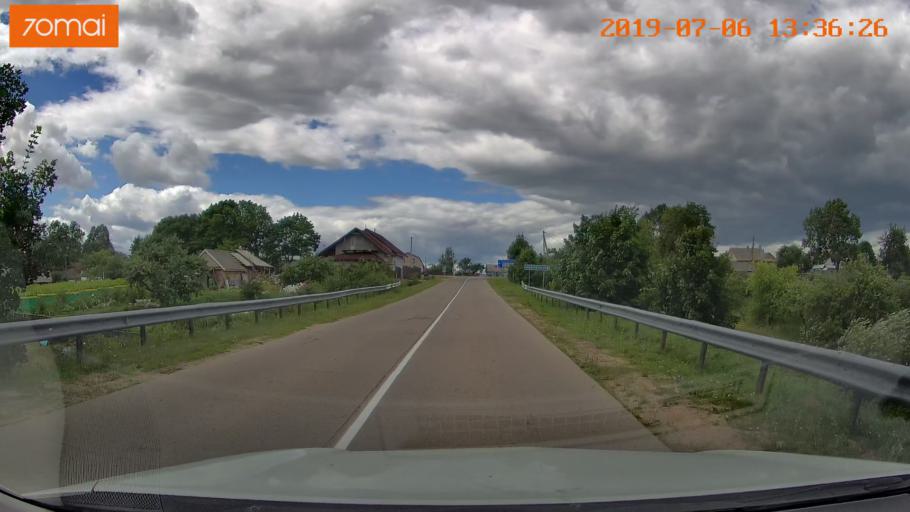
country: BY
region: Minsk
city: Enyerhyetykaw
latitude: 53.6896
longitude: 26.8663
